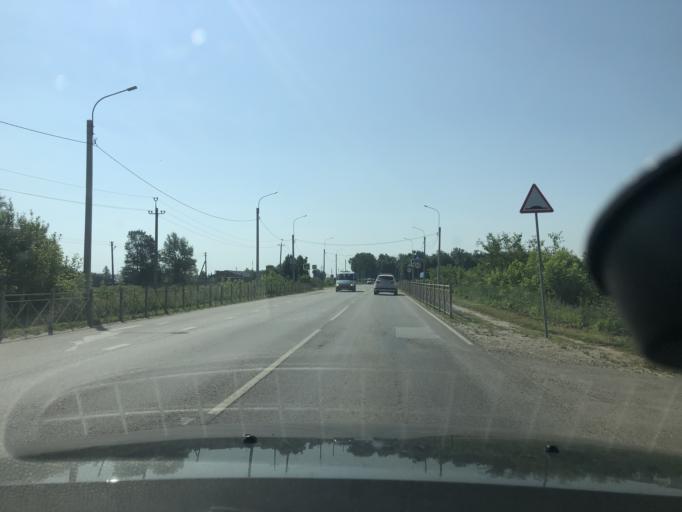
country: RU
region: Tula
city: Dubna
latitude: 54.1070
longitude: 37.1071
